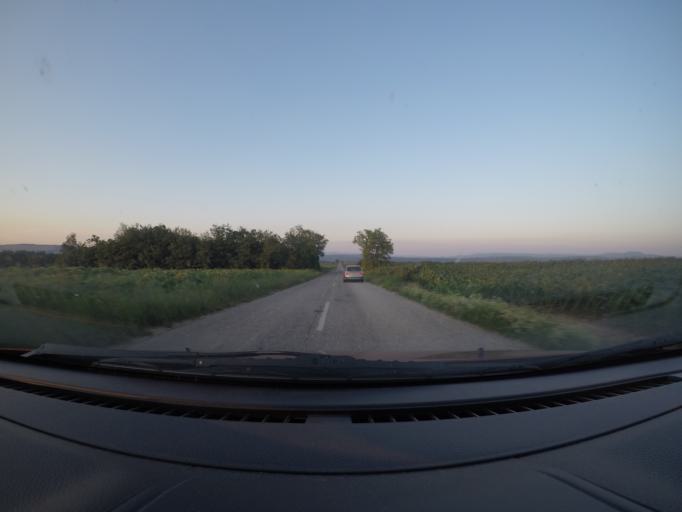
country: RS
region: Central Serbia
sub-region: Branicevski Okrug
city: Veliko Gradiste
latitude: 44.6454
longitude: 21.4555
